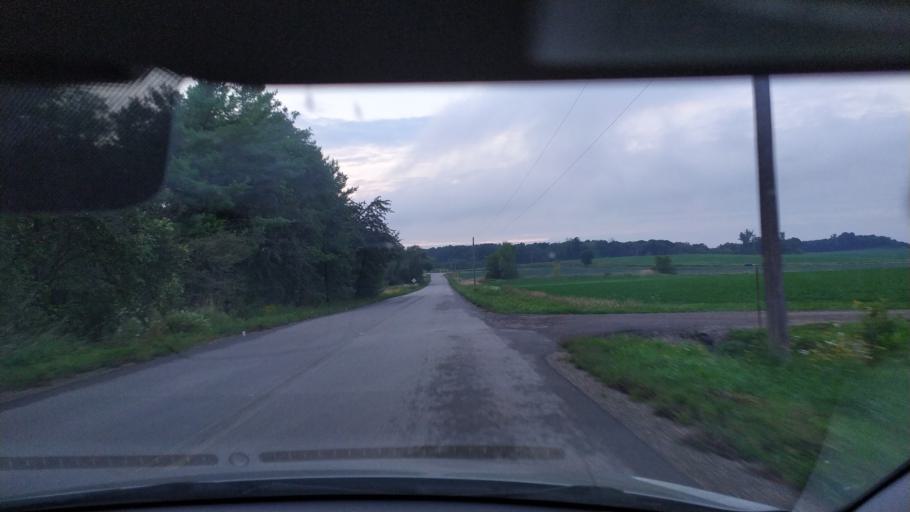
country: CA
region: Ontario
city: Kitchener
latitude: 43.3546
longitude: -80.6472
